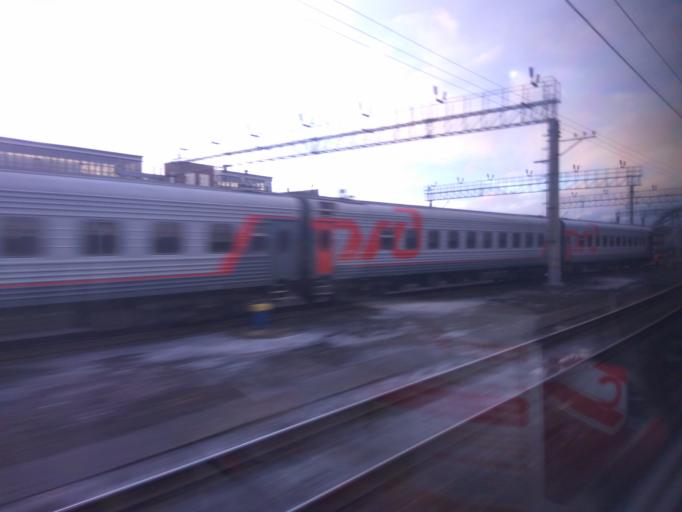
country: RU
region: St.-Petersburg
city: Centralniy
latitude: 59.9113
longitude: 30.3686
